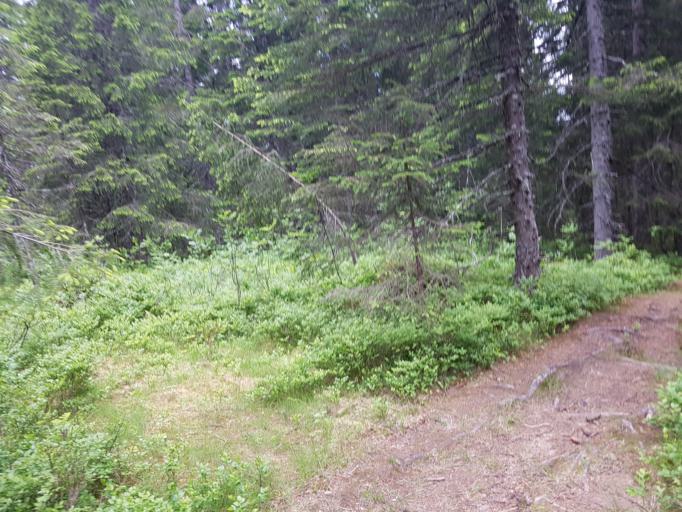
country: NO
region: Sor-Trondelag
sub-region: Trondheim
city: Trondheim
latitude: 63.4091
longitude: 10.3237
